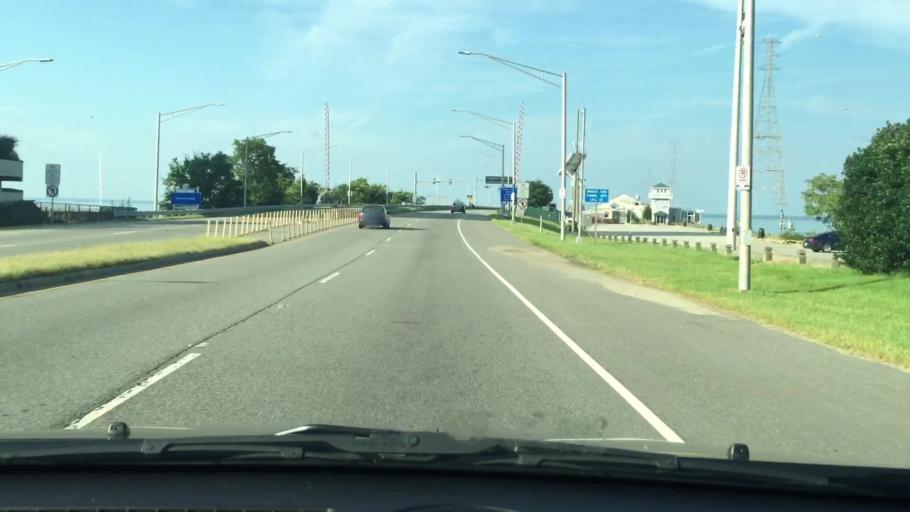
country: US
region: Virginia
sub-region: City of Newport News
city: Newport News
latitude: 37.0147
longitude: -76.4546
